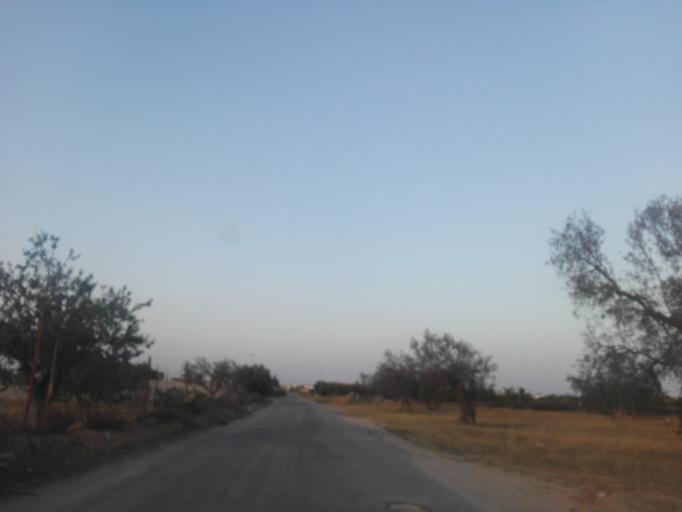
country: TN
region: Safaqis
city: Sfax
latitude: 34.7101
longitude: 10.6327
